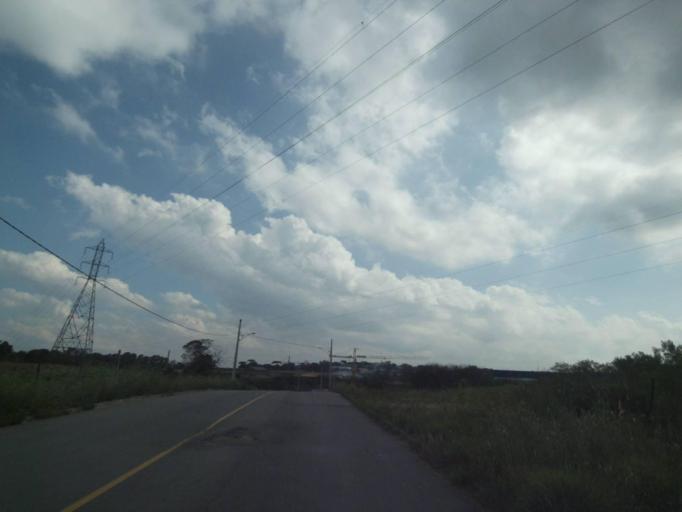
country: BR
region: Parana
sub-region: Curitiba
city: Curitiba
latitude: -25.5103
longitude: -49.3401
